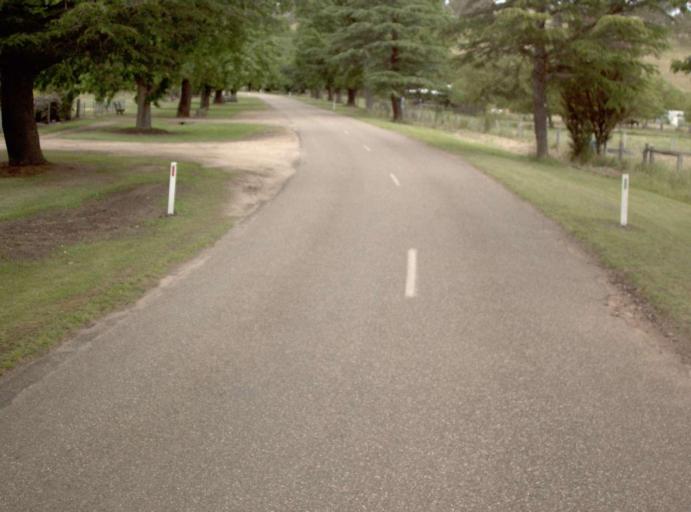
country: AU
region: Victoria
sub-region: East Gippsland
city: Bairnsdale
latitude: -37.4642
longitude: 147.2503
